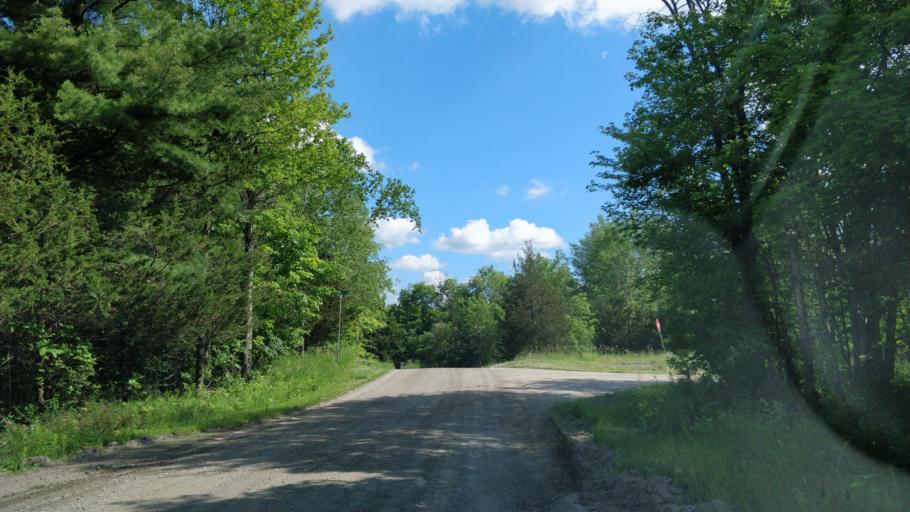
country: CA
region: Ontario
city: Perth
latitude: 44.6822
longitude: -76.5362
